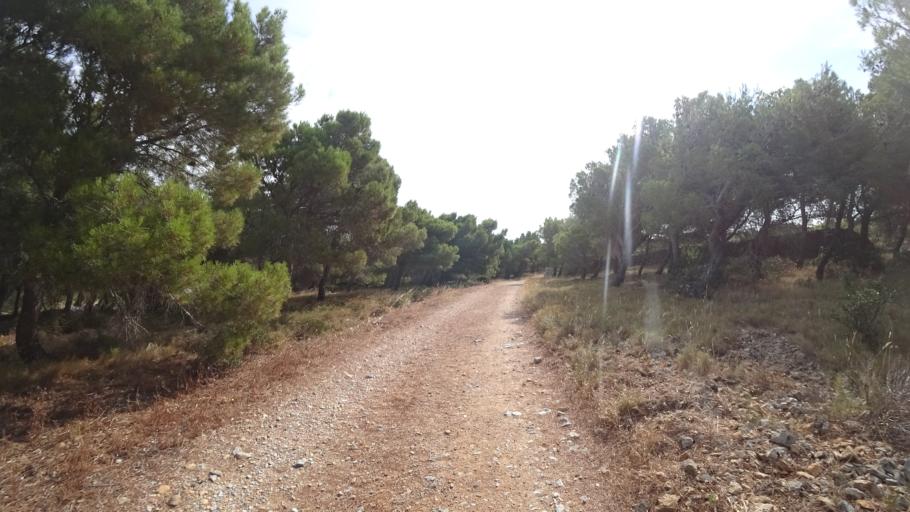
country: FR
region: Languedoc-Roussillon
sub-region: Departement de l'Aude
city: Leucate
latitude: 42.8981
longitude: 3.0195
